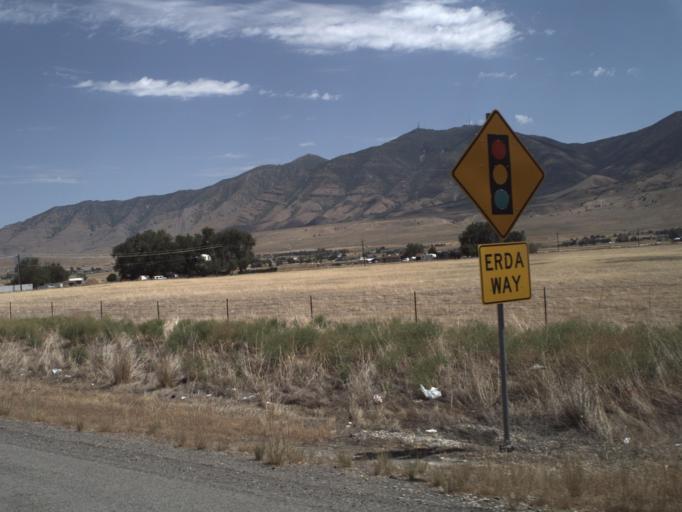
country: US
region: Utah
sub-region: Tooele County
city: Erda
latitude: 40.5965
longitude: -112.2940
